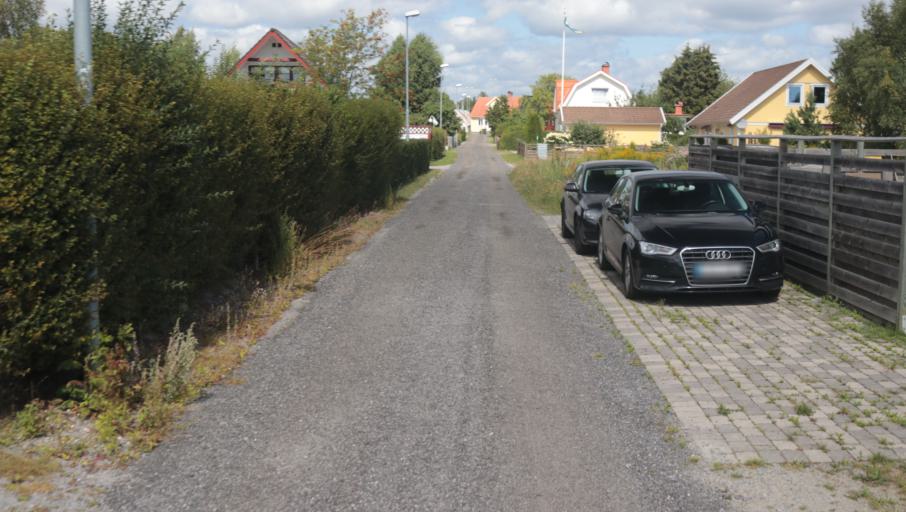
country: SE
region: Blekinge
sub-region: Karlshamns Kommun
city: Morrum
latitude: 56.1627
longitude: 14.6817
